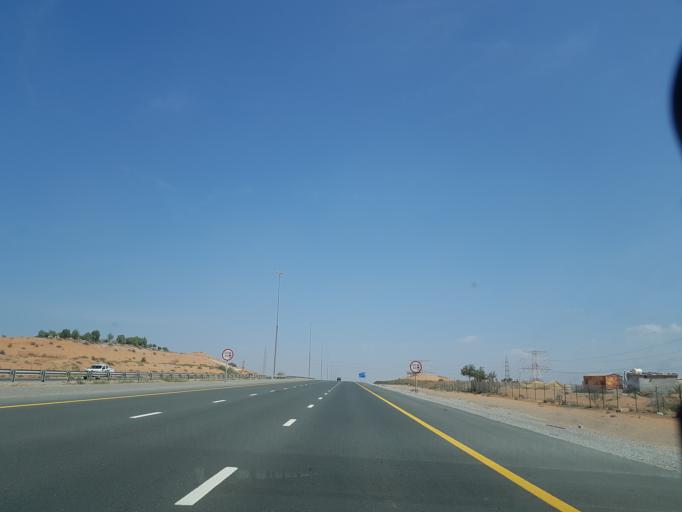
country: AE
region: Ra's al Khaymah
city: Ras al-Khaimah
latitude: 25.6878
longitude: 55.9153
